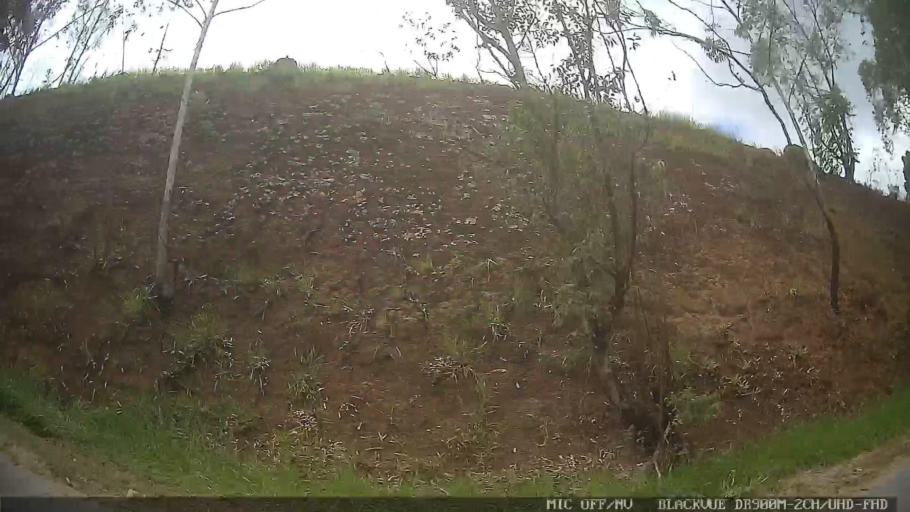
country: BR
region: Sao Paulo
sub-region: Braganca Paulista
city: Braganca Paulista
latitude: -22.8160
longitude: -46.5453
